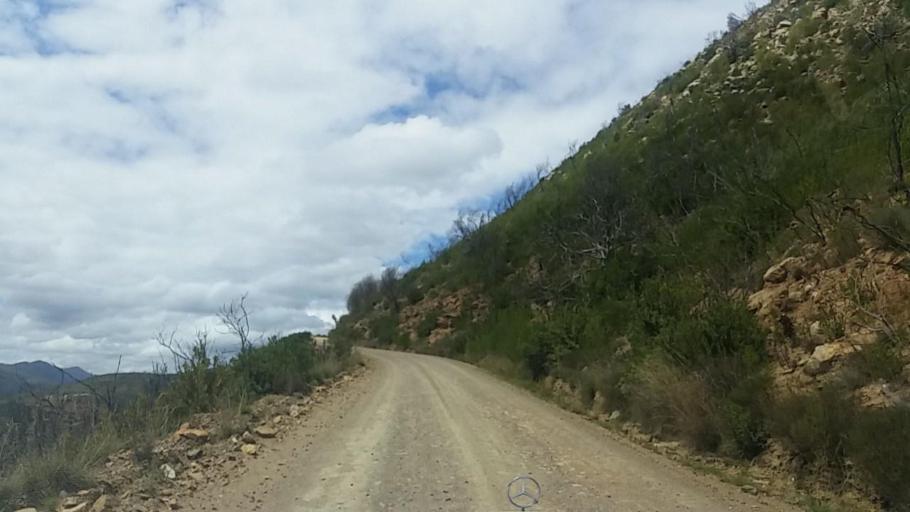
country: ZA
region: Western Cape
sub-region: Eden District Municipality
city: Knysna
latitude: -33.8214
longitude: 23.1775
